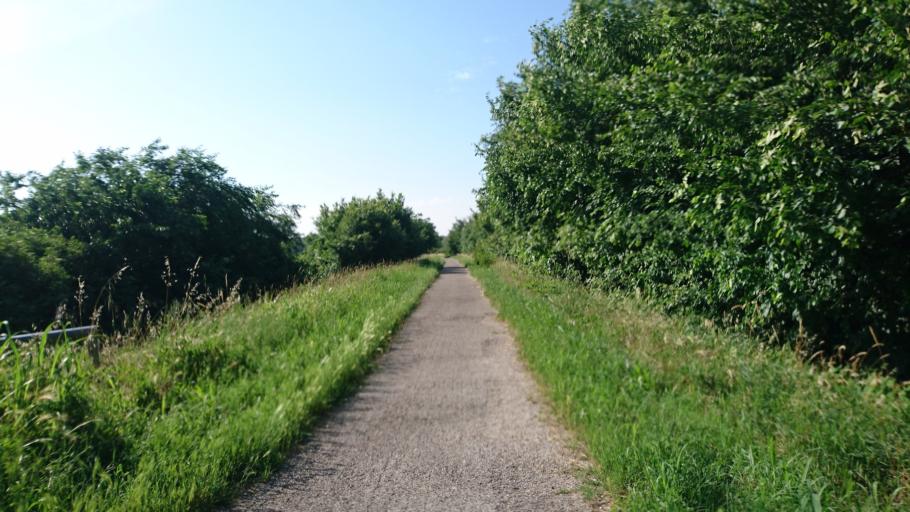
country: IT
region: Veneto
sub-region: Provincia di Verona
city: Villa Bartolomea
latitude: 45.1773
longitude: 11.3310
